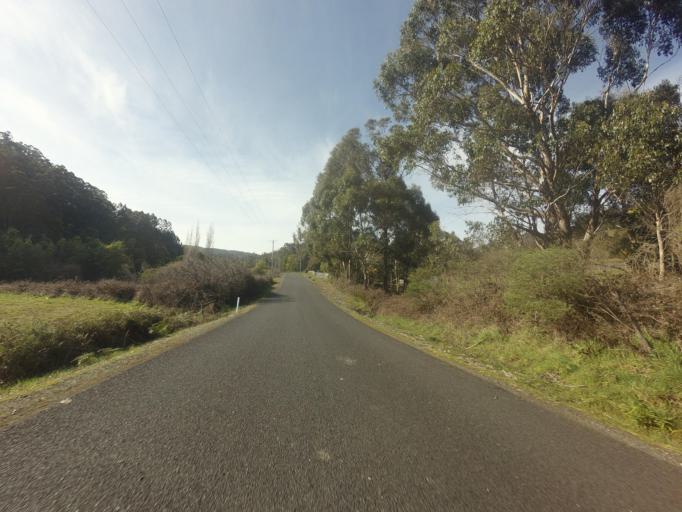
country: AU
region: Tasmania
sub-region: Huon Valley
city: Cygnet
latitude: -43.1788
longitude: 147.1436
